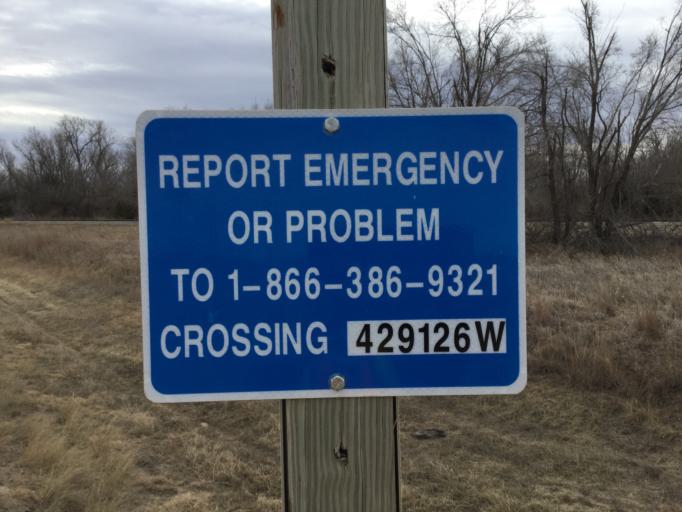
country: US
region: Kansas
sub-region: Rice County
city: Sterling
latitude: 38.2028
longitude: -98.1920
